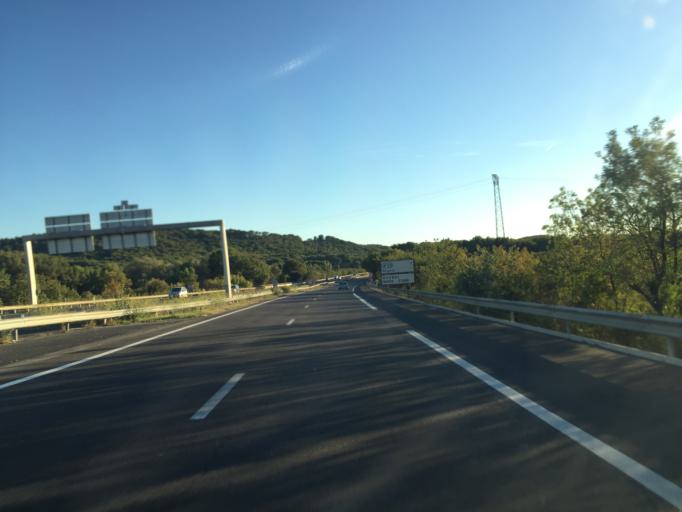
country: FR
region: Provence-Alpes-Cote d'Azur
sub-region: Departement des Bouches-du-Rhone
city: Coudoux
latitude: 43.5481
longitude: 5.2297
